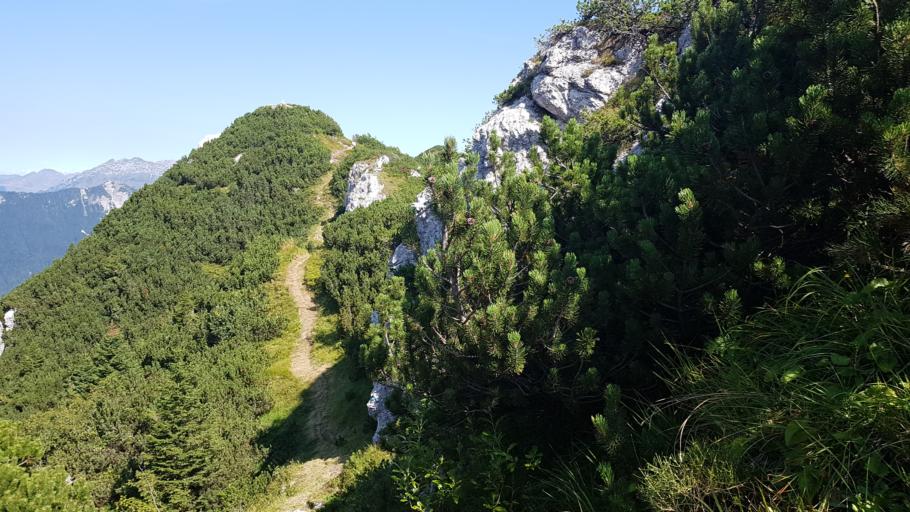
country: IT
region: Friuli Venezia Giulia
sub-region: Provincia di Udine
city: Moggio Udinese
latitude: 46.4732
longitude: 13.2185
